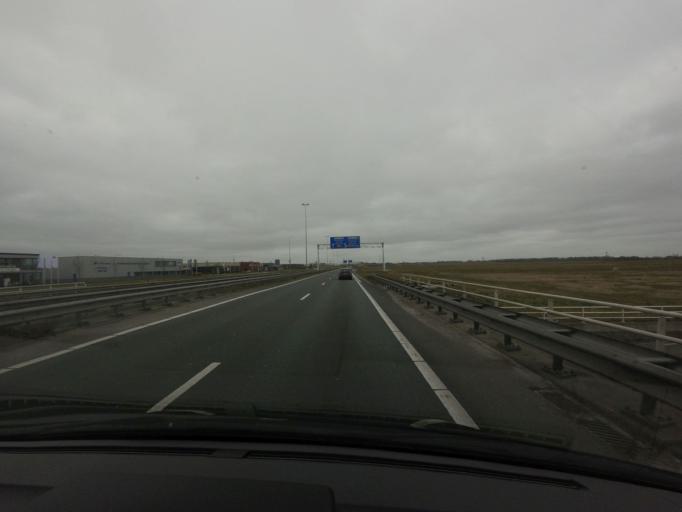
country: NL
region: Groningen
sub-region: Gemeente Haren
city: Haren
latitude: 53.2098
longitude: 6.6259
